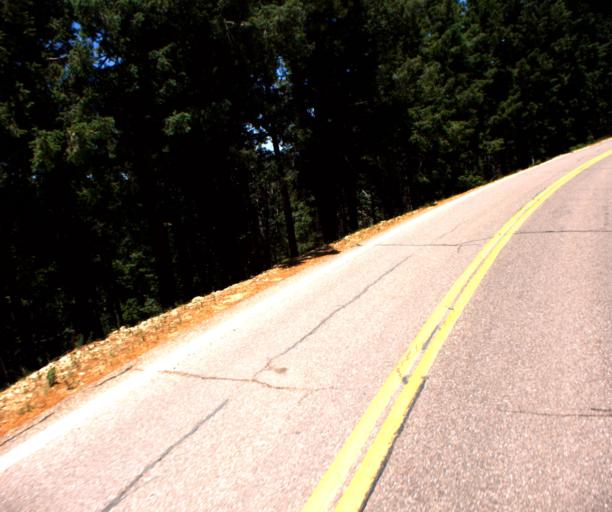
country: US
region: Arizona
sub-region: Graham County
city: Swift Trail Junction
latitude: 32.6580
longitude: -109.8653
